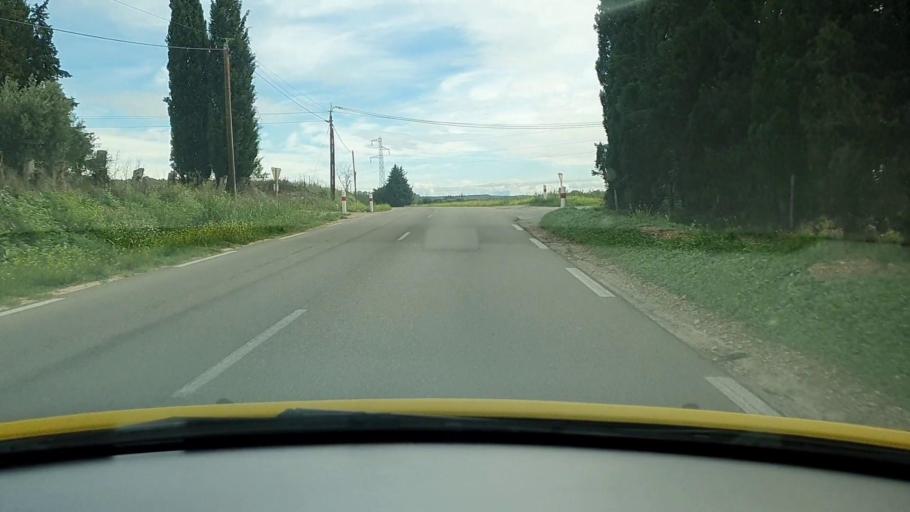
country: FR
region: Languedoc-Roussillon
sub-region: Departement du Gard
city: Bellegarde
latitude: 43.7722
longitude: 4.5361
